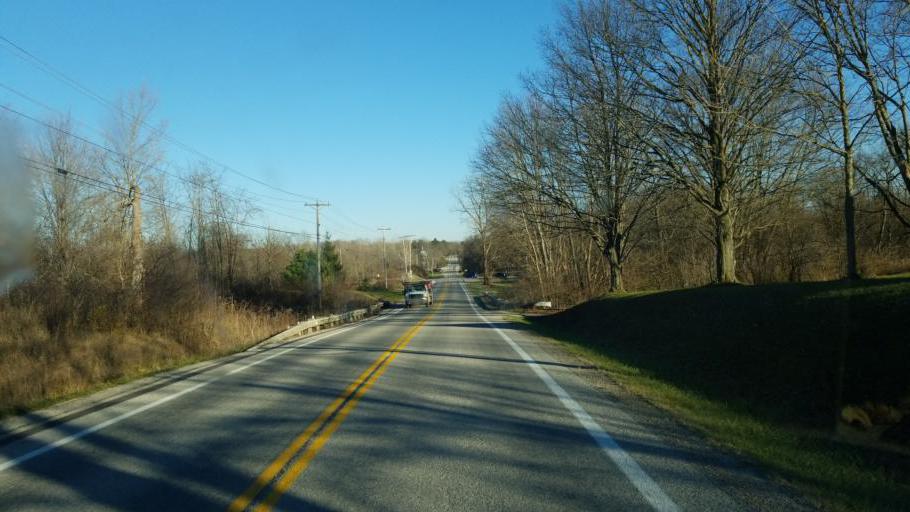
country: US
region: Ohio
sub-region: Delaware County
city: Ashley
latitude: 40.4064
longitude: -82.8680
